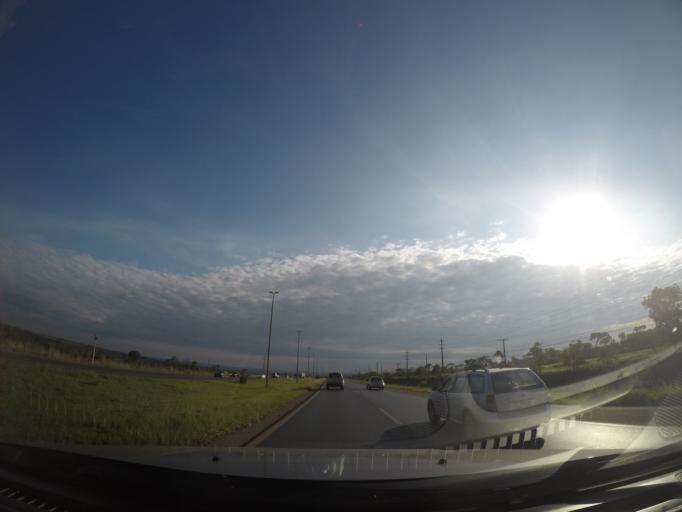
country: BR
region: Goias
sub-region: Planaltina
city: Planaltina
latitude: -15.6364
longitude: -47.7437
